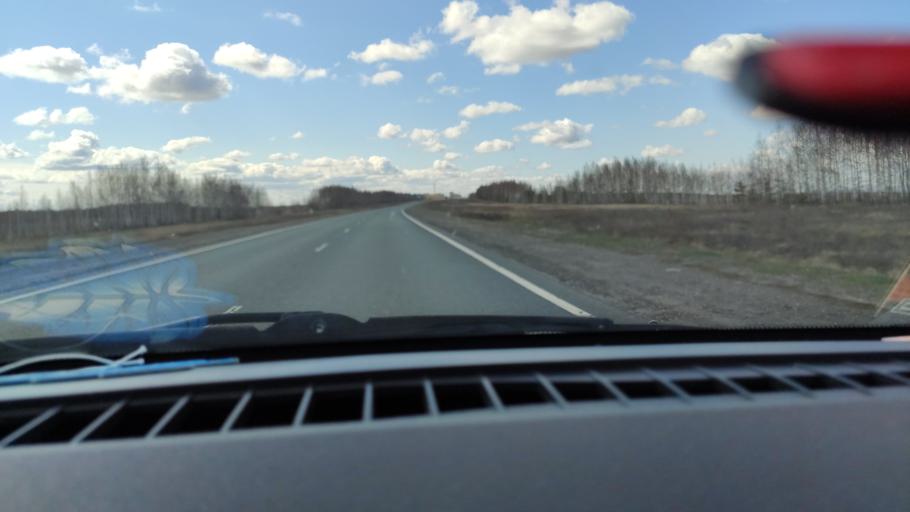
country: RU
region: Saratov
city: Dukhovnitskoye
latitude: 52.8459
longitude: 48.2524
